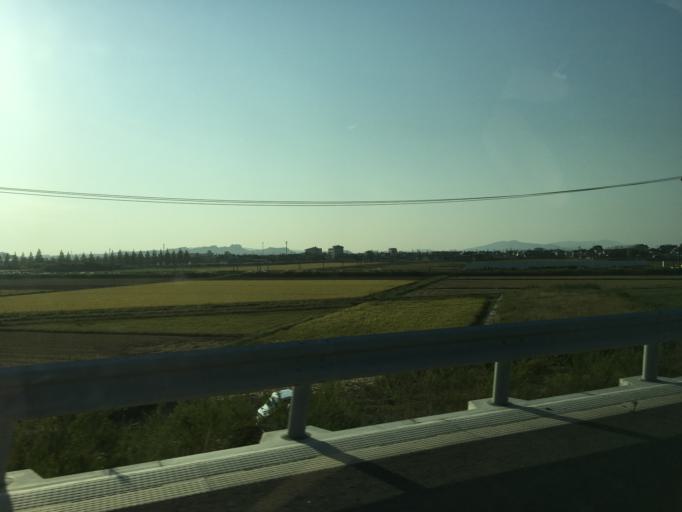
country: JP
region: Miyagi
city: Ishinomaki
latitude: 38.4832
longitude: 141.2923
